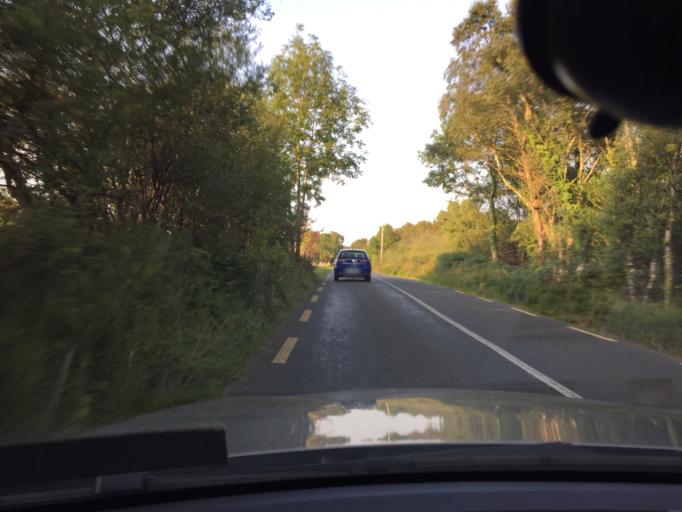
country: IE
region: Leinster
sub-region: Wicklow
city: Rathdrum
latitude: 53.0461
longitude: -6.2448
